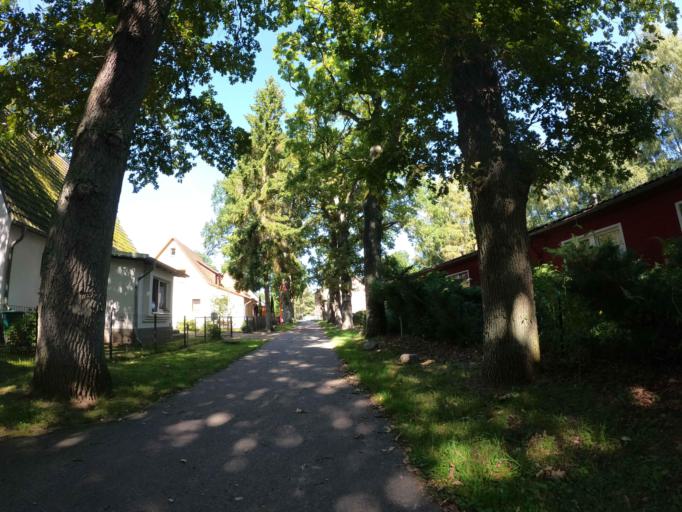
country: DE
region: Mecklenburg-Vorpommern
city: Prohn
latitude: 54.4321
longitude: 13.0311
